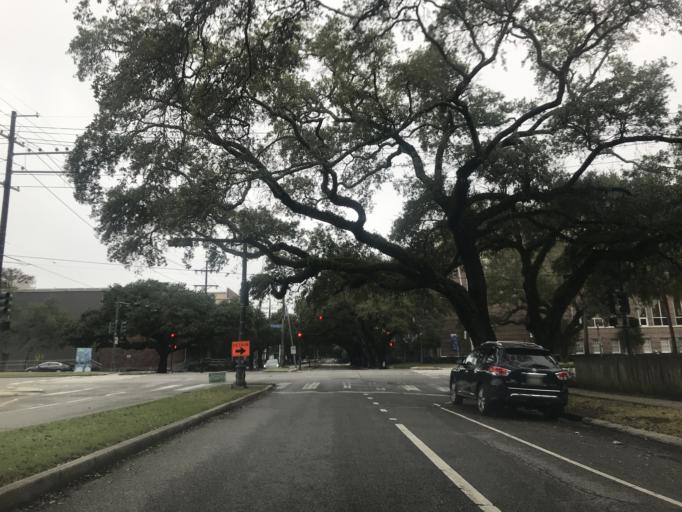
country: US
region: Louisiana
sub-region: Orleans Parish
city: New Orleans
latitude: 29.9718
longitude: -90.1028
